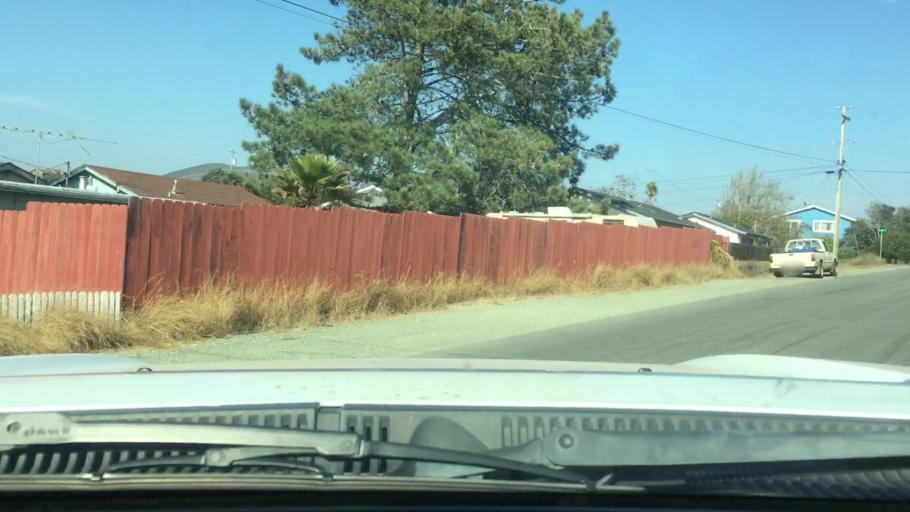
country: US
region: California
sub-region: San Luis Obispo County
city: Los Osos
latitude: 35.3244
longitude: -120.8309
